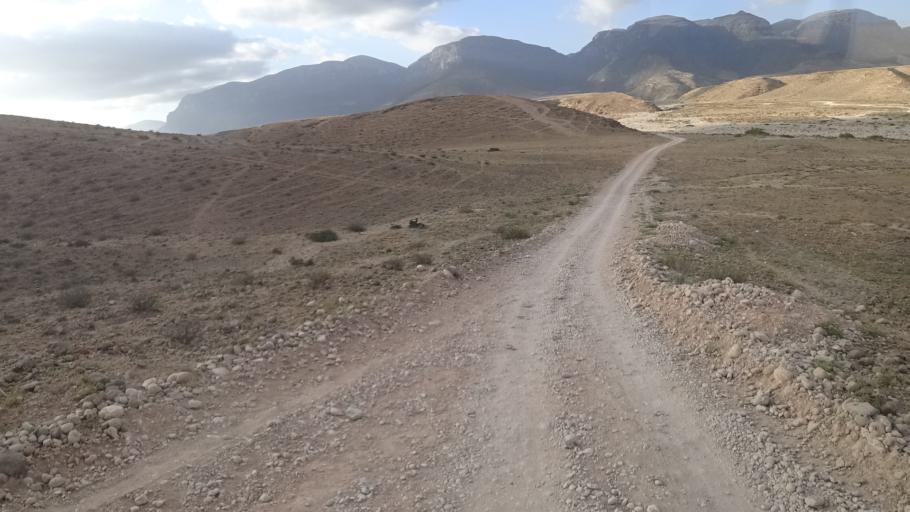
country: OM
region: Zufar
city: Salalah
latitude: 16.9749
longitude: 53.8529
